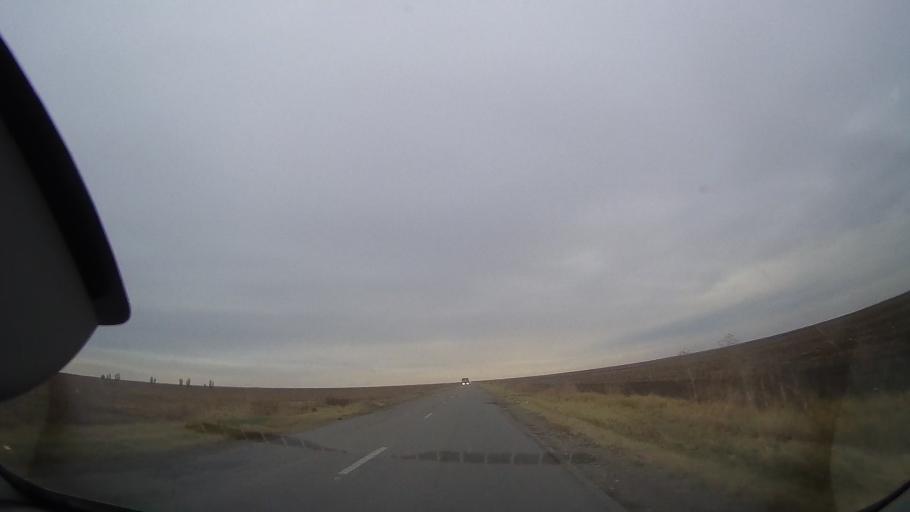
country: RO
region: Ialomita
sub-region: Oras Amara
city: Amara
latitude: 44.6493
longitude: 27.3006
